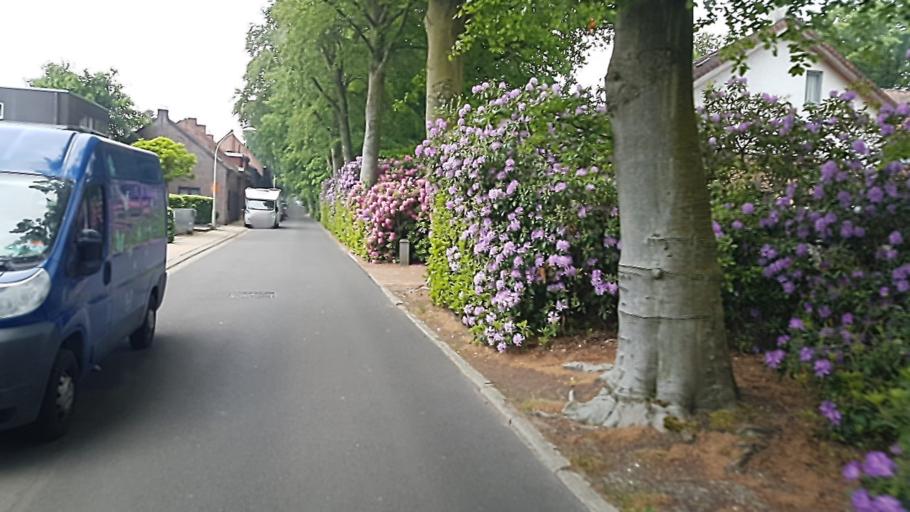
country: BE
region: Flanders
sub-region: Provincie Antwerpen
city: Kapellen
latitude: 51.3259
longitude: 4.4362
